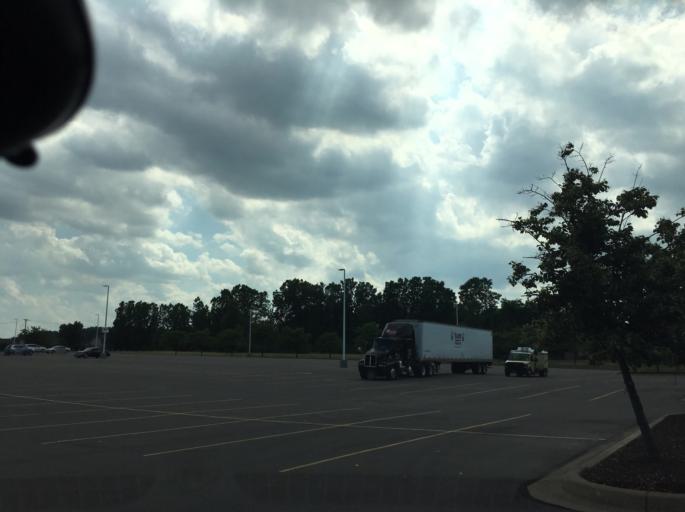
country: US
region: Michigan
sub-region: Macomb County
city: Fraser
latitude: 42.5525
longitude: -82.9634
